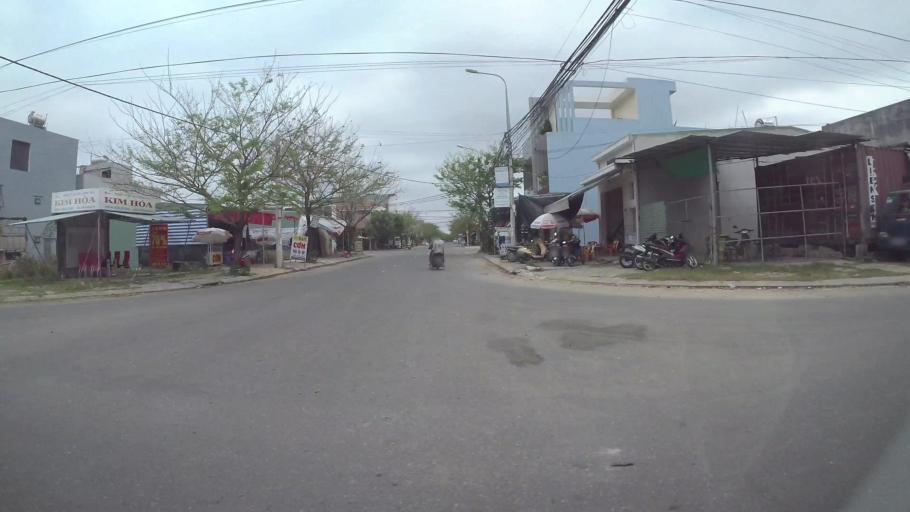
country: VN
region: Da Nang
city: Lien Chieu
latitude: 16.0454
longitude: 108.1679
